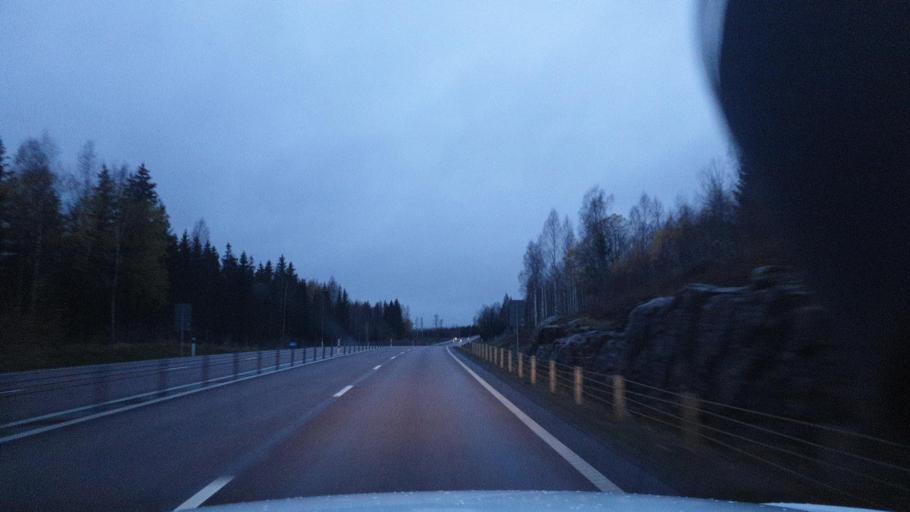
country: SE
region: Vaermland
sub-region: Eda Kommun
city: Amotfors
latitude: 59.7574
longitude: 12.4208
